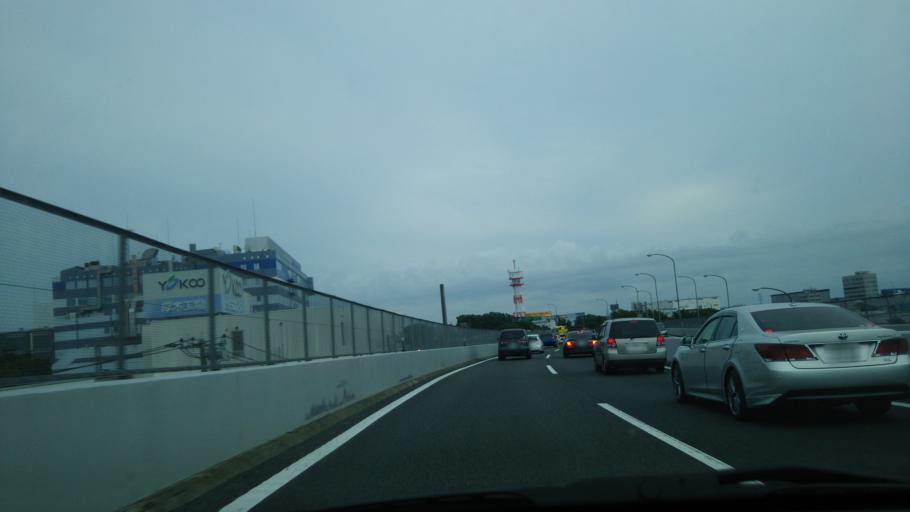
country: JP
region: Kanagawa
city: Atsugi
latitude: 35.4193
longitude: 139.3555
